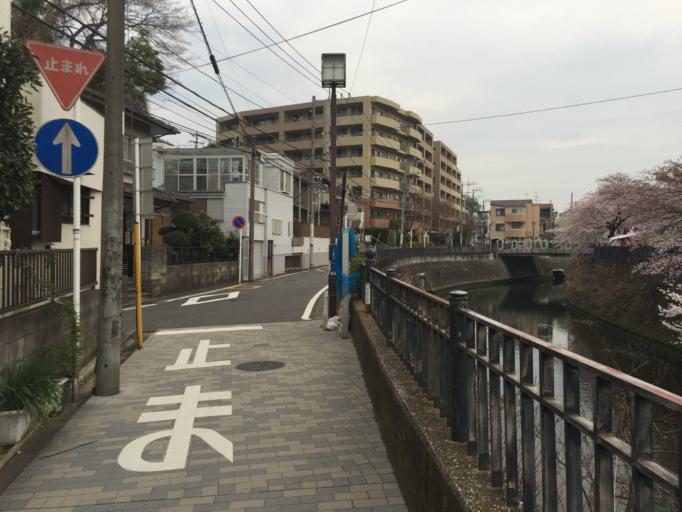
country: JP
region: Kanagawa
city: Yokohama
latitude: 35.4254
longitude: 139.5998
